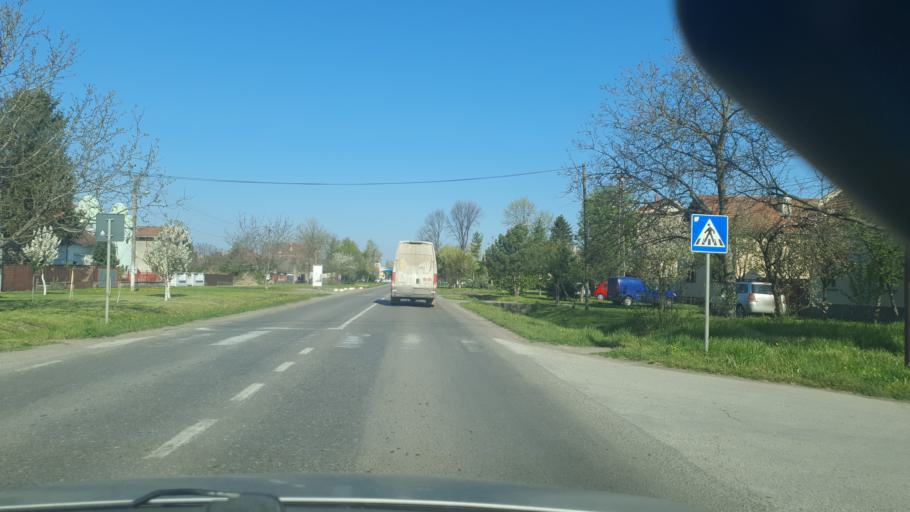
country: RS
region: Autonomna Pokrajina Vojvodina
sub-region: Zapadnobacki Okrug
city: Kula
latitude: 45.6614
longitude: 19.4500
